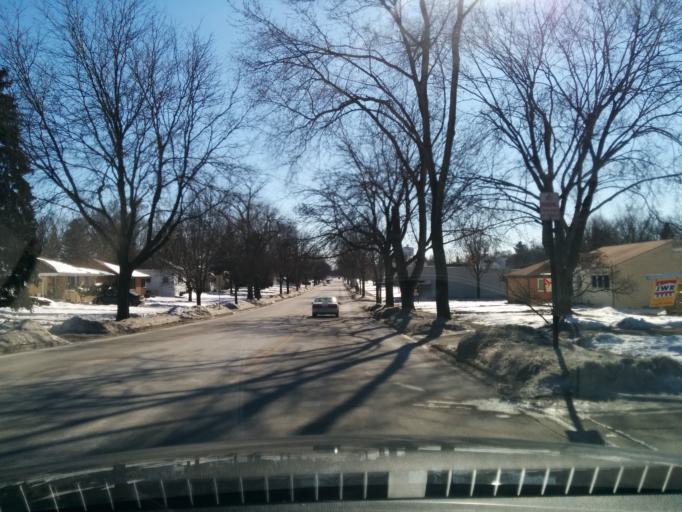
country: US
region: Illinois
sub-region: DuPage County
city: Villa Park
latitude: 41.8954
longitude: -87.9791
